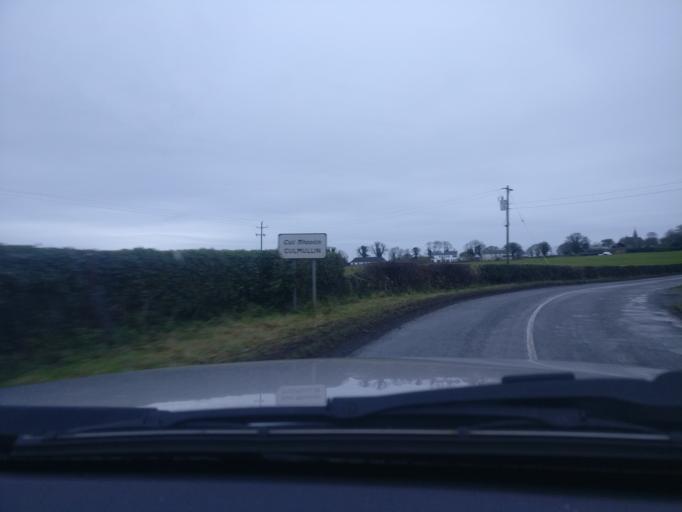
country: IE
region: Leinster
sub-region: An Mhi
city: Dunshaughlin
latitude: 53.4942
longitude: -6.6025
